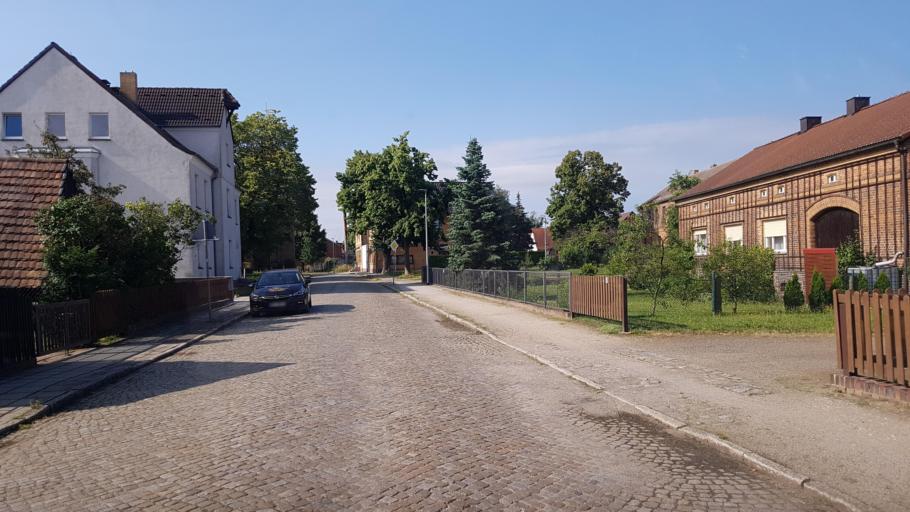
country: DE
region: Brandenburg
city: Grossraschen
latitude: 51.5514
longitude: 14.0581
